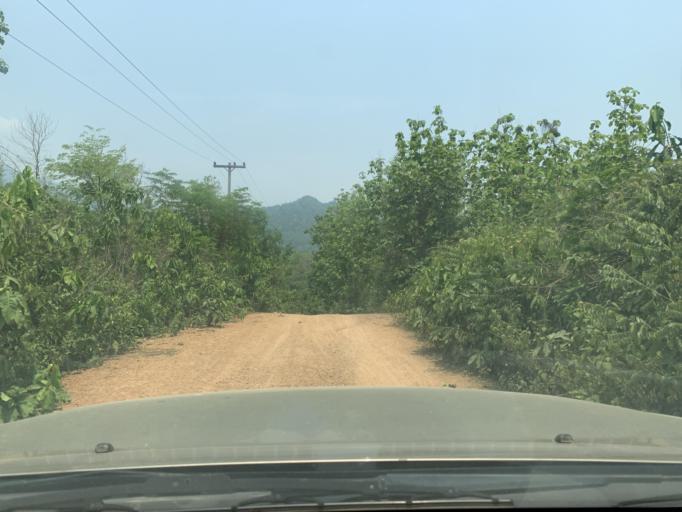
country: LA
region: Louangphabang
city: Louangphabang
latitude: 19.9655
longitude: 102.1268
